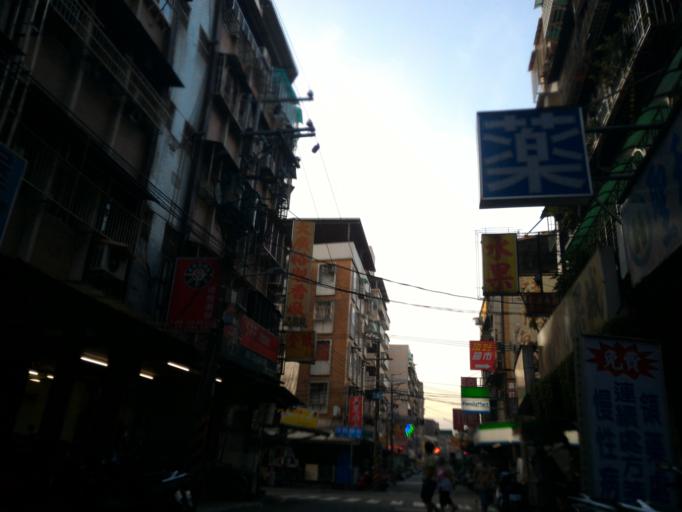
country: TW
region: Taipei
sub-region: Taipei
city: Banqiao
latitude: 24.9797
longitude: 121.4184
